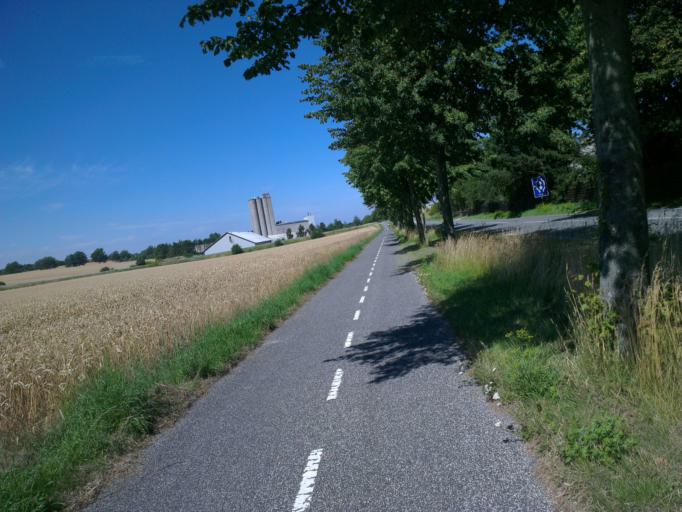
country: DK
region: Capital Region
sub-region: Frederikssund Kommune
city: Slangerup
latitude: 55.8304
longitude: 12.1863
